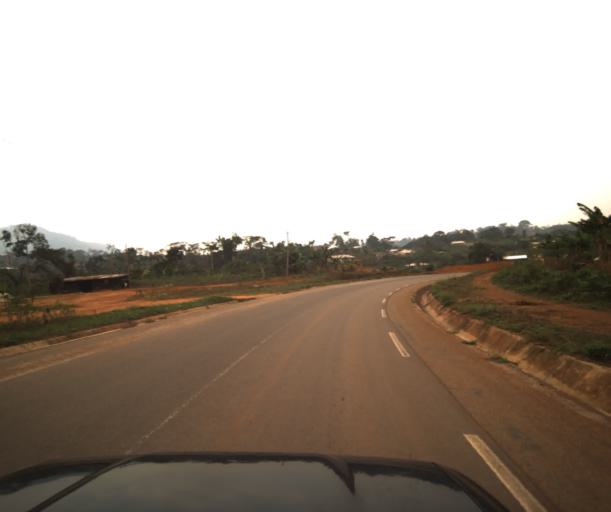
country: CM
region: Centre
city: Mbankomo
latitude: 3.7962
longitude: 11.4495
